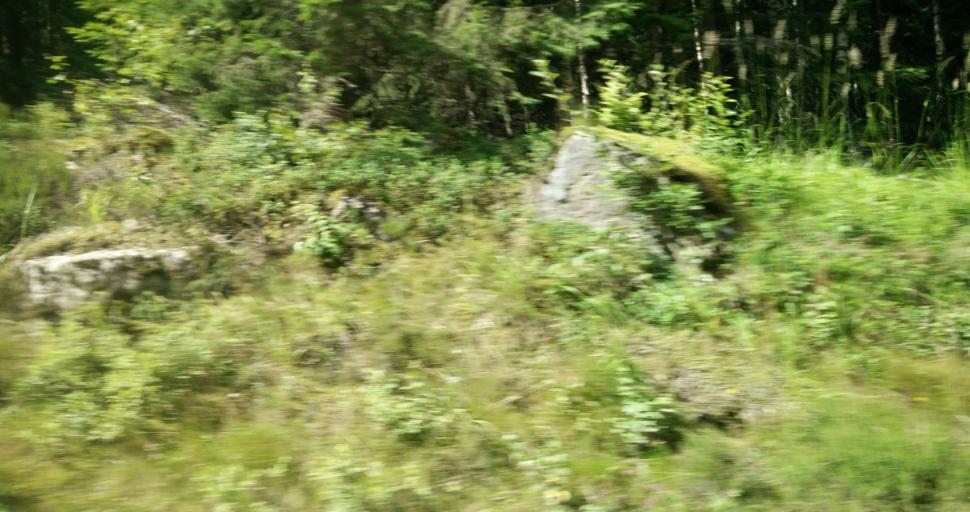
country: SE
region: Vaermland
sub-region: Hagfors Kommun
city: Ekshaerad
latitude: 60.0936
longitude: 13.4497
